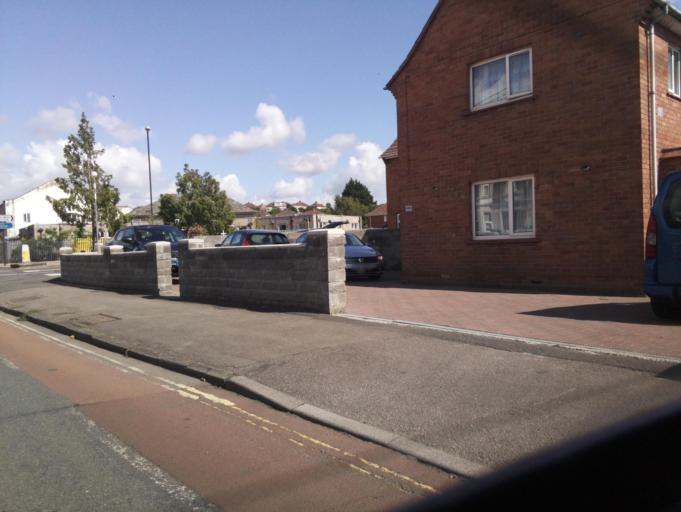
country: GB
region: England
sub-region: Bristol
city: Bristol
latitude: 51.4365
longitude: -2.5898
